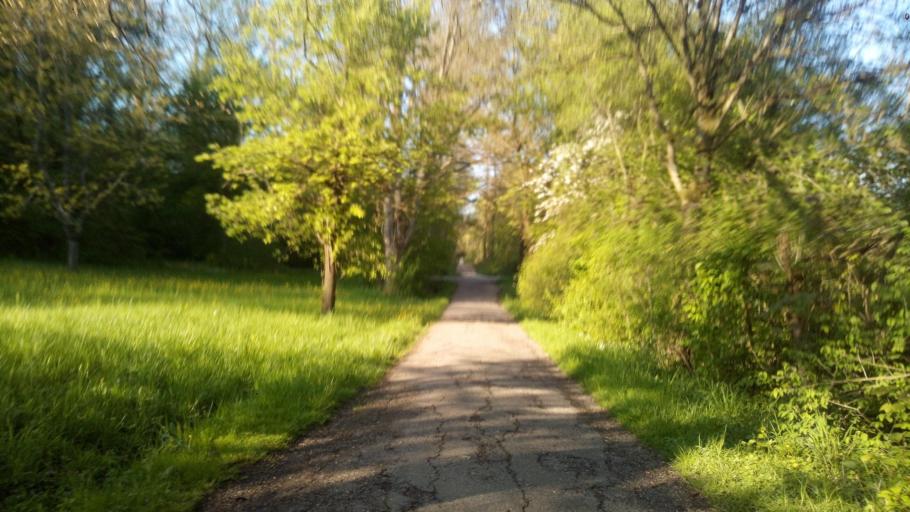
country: DE
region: Baden-Wuerttemberg
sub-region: Regierungsbezirk Stuttgart
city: Goeppingen
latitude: 48.7129
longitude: 9.6729
